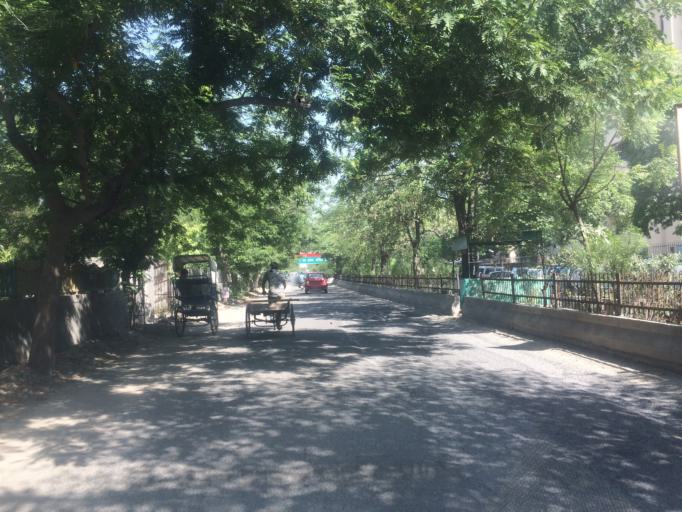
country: IN
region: Uttar Pradesh
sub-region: Gautam Buddha Nagar
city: Noida
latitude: 28.5753
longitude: 77.3690
